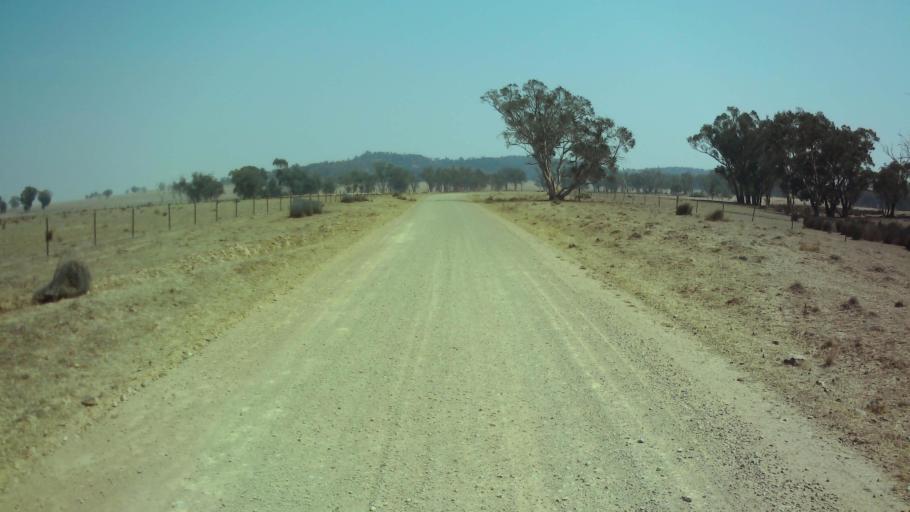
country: AU
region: New South Wales
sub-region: Weddin
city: Grenfell
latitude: -33.6773
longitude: 148.2763
